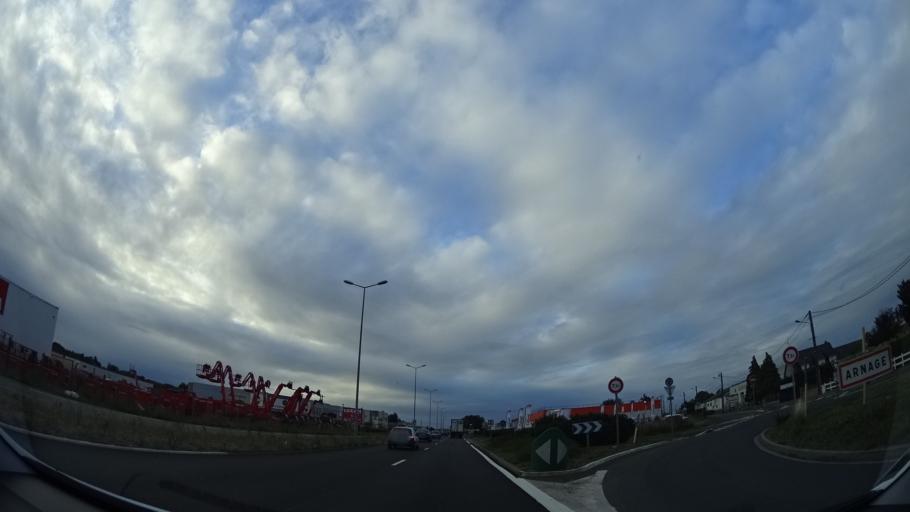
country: FR
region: Pays de la Loire
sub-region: Departement de la Sarthe
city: Arnage
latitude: 47.9498
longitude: 0.1812
